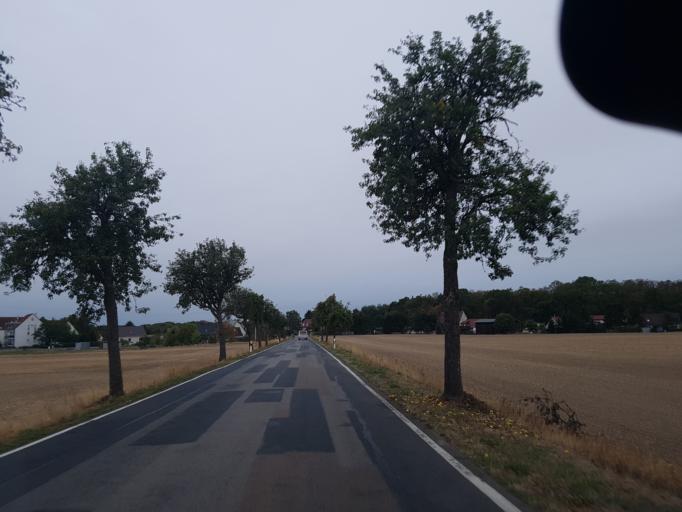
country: DE
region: Saxony
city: Arzberg
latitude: 51.5371
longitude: 13.1029
